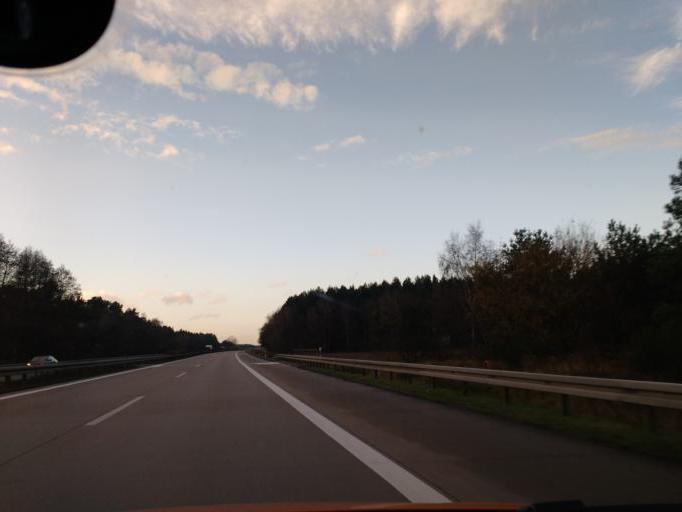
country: DE
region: Mecklenburg-Vorpommern
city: Rastow
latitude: 53.4435
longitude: 11.3756
